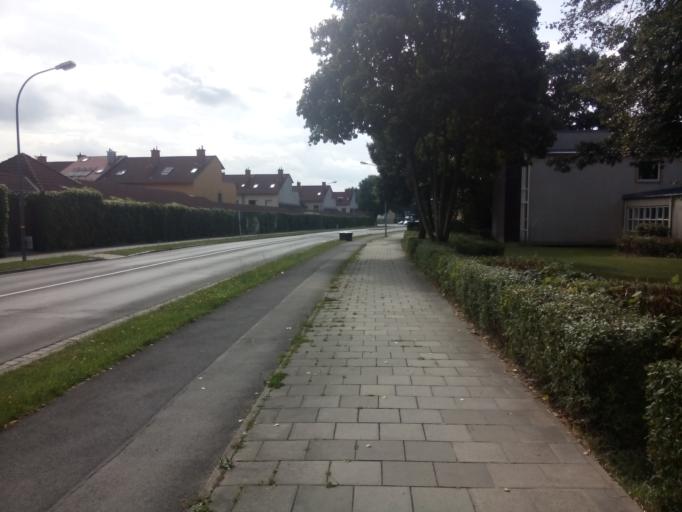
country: DE
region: Bavaria
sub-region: Upper Franconia
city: Bamberg
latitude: 49.8849
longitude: 10.9107
